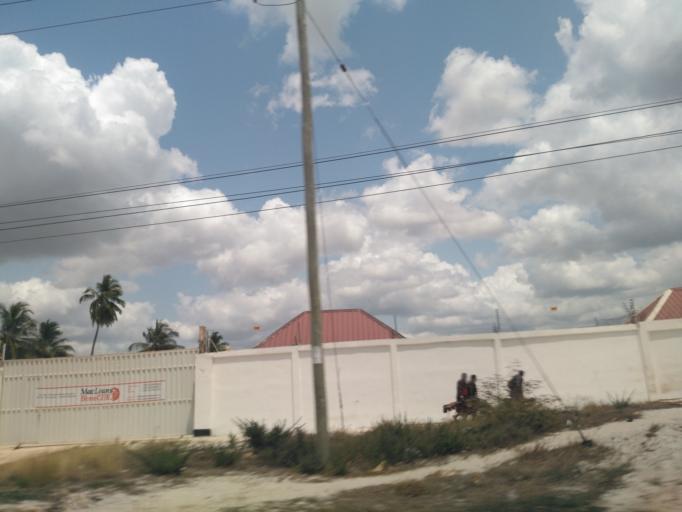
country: TZ
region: Dar es Salaam
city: Dar es Salaam
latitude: -6.8743
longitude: 39.3440
